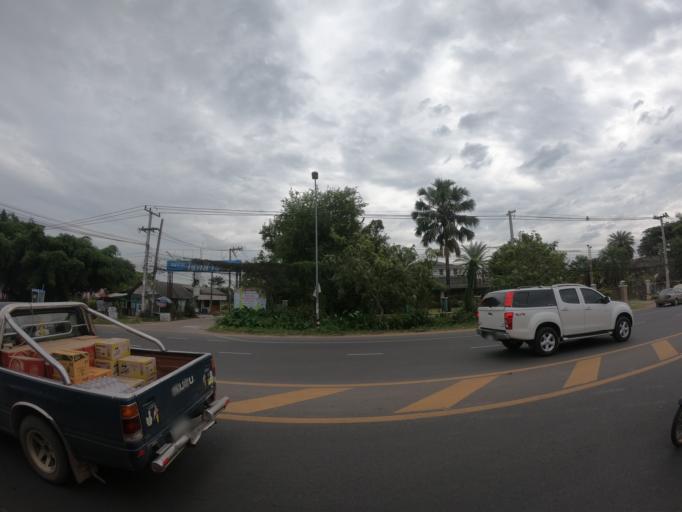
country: TH
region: Roi Et
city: Roi Et
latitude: 16.0668
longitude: 103.6723
